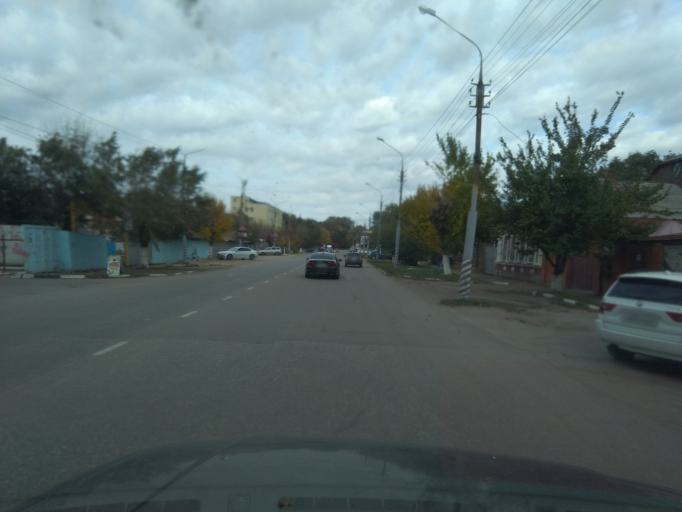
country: RU
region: Saratov
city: Engel's
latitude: 51.4917
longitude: 46.1233
